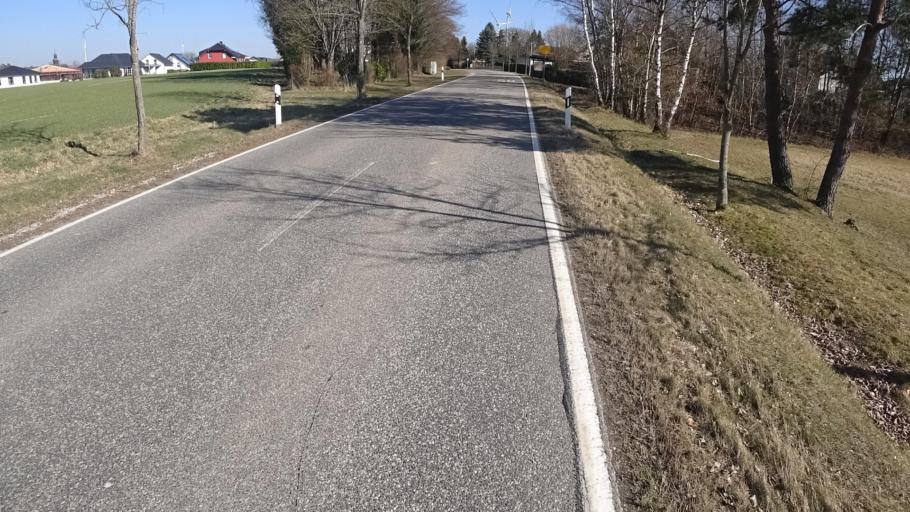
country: DE
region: Rheinland-Pfalz
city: Mutterschied
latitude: 49.9942
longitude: 7.5617
